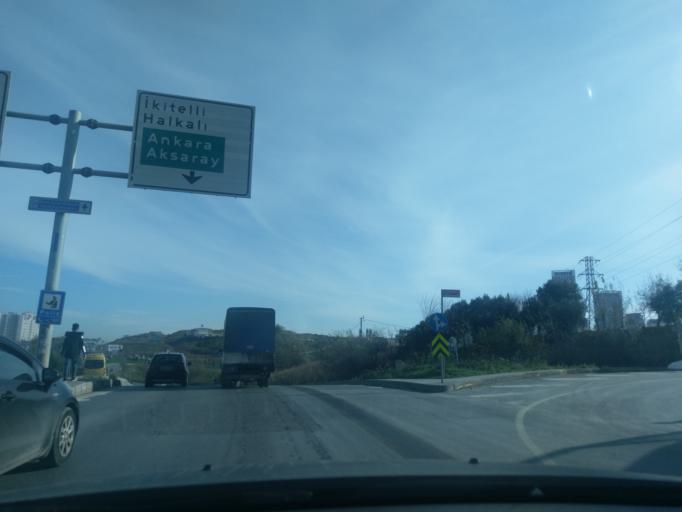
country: TR
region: Istanbul
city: Basaksehir
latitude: 41.0603
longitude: 28.7538
